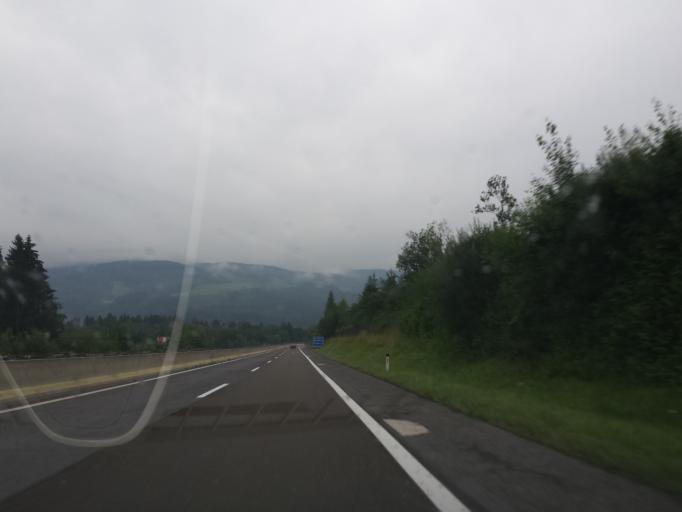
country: AT
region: Styria
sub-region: Politischer Bezirk Bruck-Muerzzuschlag
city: Krieglach
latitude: 47.5516
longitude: 15.5775
